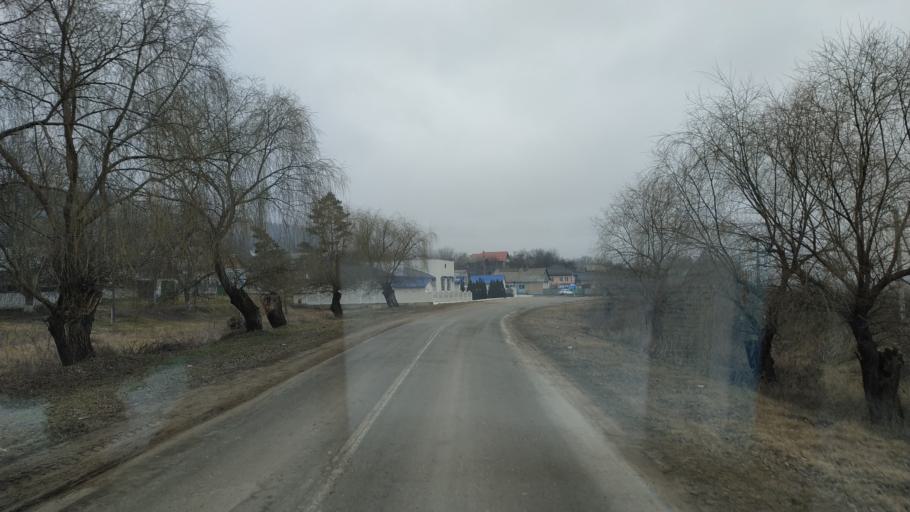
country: MD
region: Hincesti
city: Hincesti
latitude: 46.9584
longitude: 28.4877
